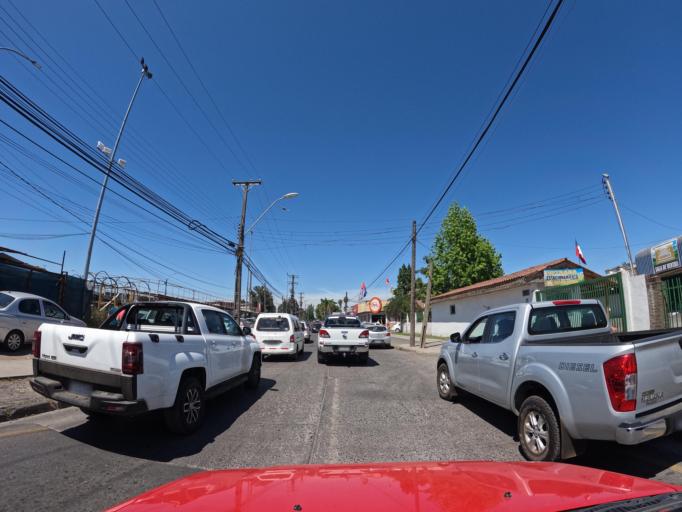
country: CL
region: Maule
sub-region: Provincia de Curico
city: Curico
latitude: -34.9831
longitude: -71.2493
